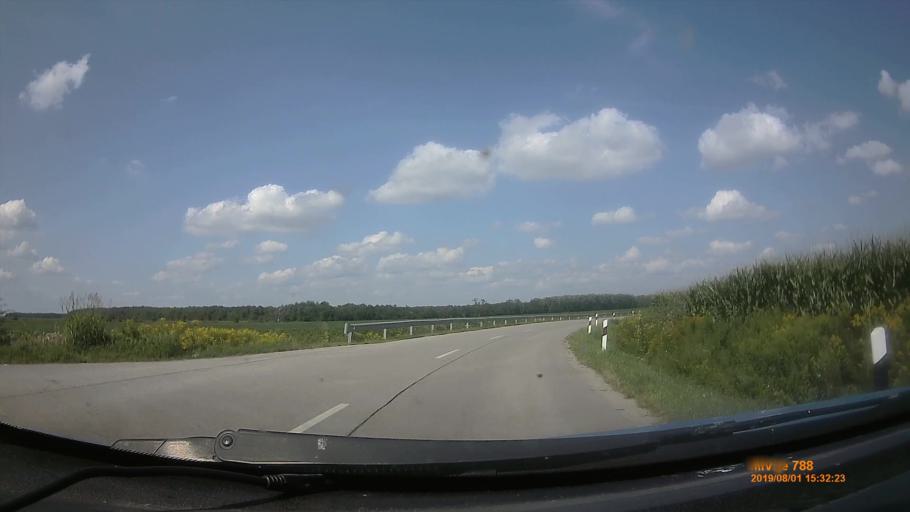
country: HU
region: Baranya
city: Sellye
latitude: 45.9490
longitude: 17.8631
